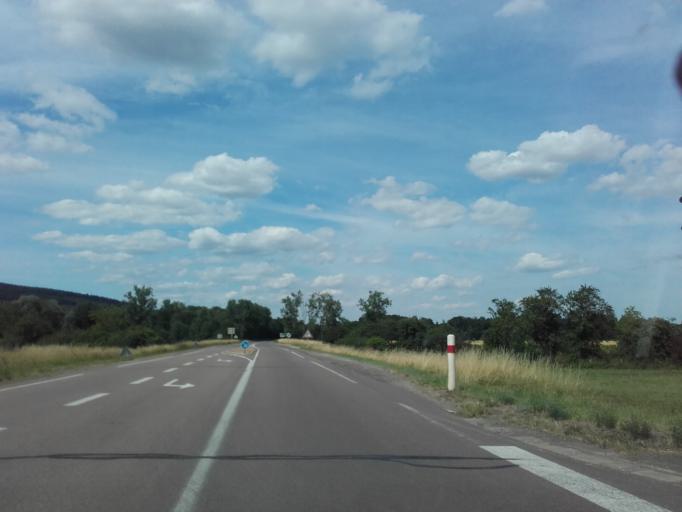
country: FR
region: Bourgogne
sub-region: Departement de Saone-et-Loire
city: Chagny
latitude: 46.9077
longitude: 4.7114
